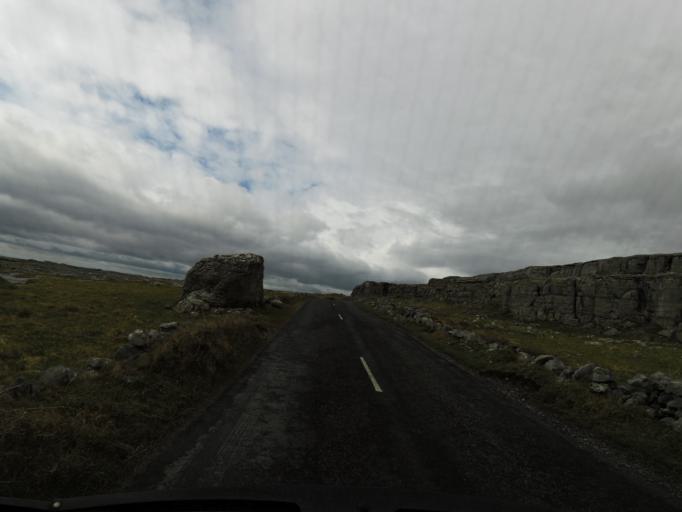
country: IE
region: Connaught
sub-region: County Galway
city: Bearna
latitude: 53.0657
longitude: -9.3593
